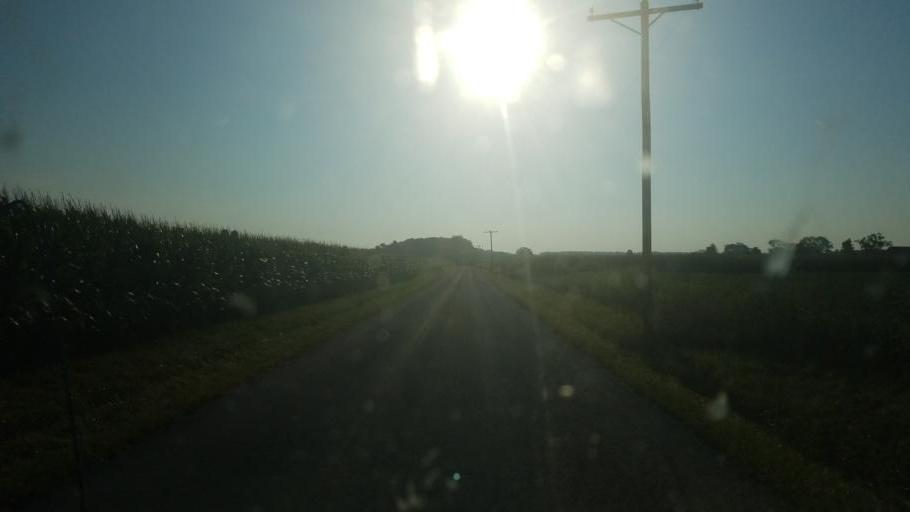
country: US
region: Ohio
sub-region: Huron County
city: Greenwich
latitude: 40.9095
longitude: -82.4606
